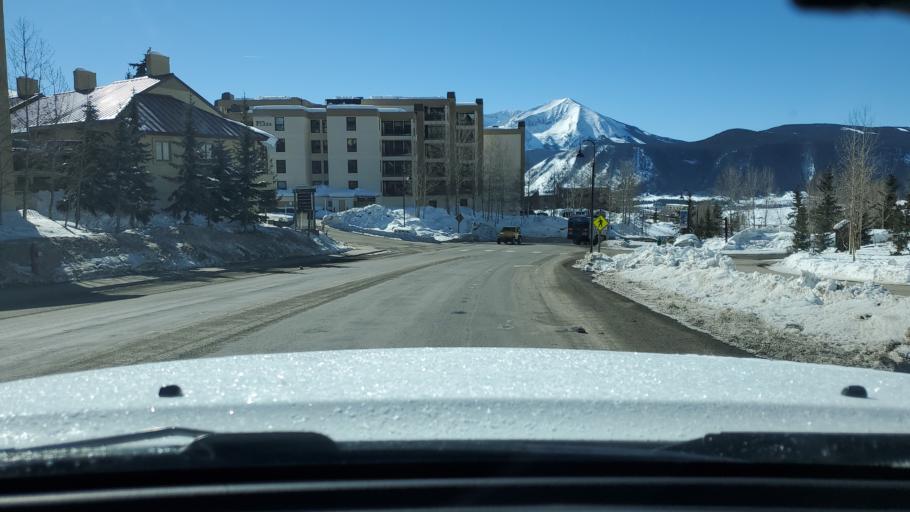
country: US
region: Colorado
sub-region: Gunnison County
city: Crested Butte
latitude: 38.8991
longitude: -106.9672
